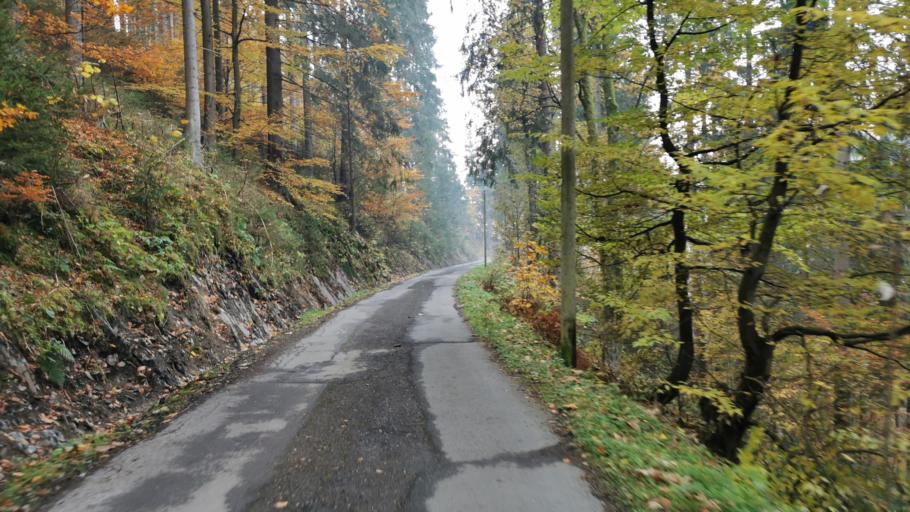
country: DE
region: Bavaria
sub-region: Upper Franconia
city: Nordhalben
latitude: 50.3752
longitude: 11.5267
